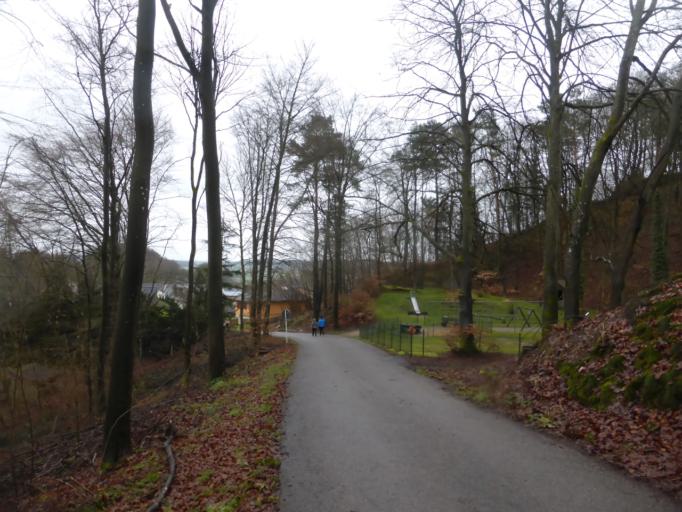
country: LU
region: Luxembourg
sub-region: Canton de Mersch
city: Lorentzweiler
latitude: 49.7020
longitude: 6.1631
